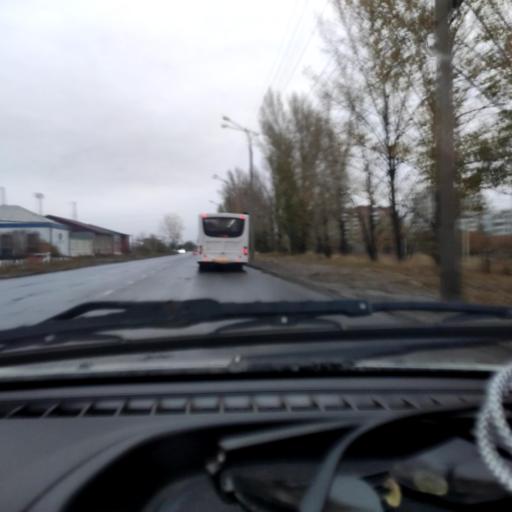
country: RU
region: Samara
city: Zhigulevsk
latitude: 53.4766
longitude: 49.5262
